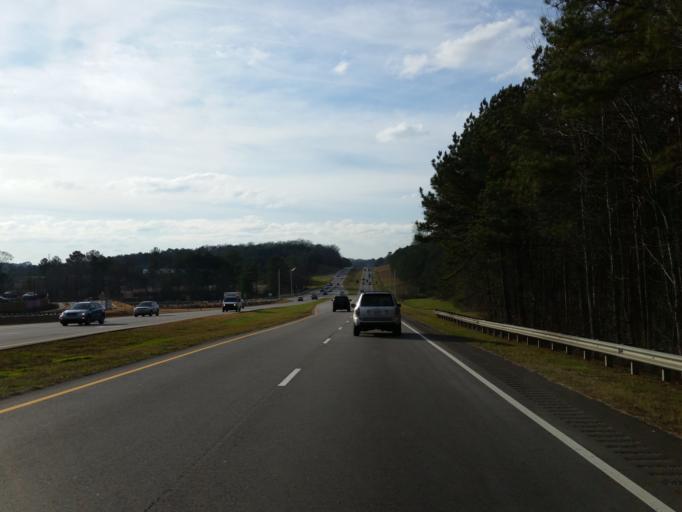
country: US
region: Georgia
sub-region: Paulding County
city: Hiram
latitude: 33.9026
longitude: -84.7799
